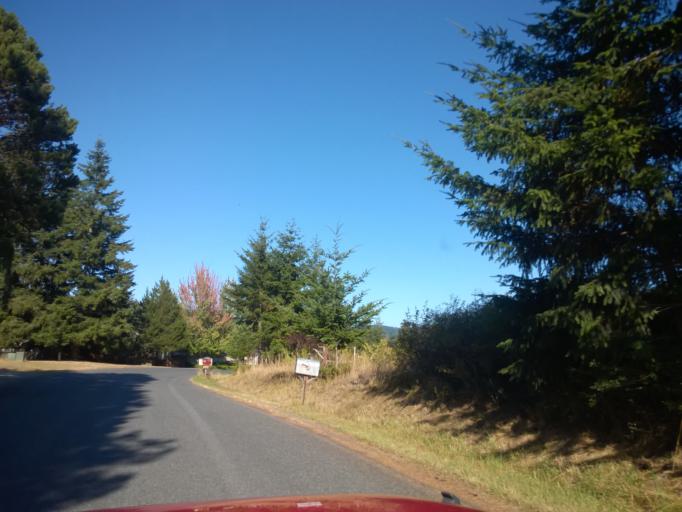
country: US
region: Washington
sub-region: San Juan County
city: Friday Harbor
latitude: 48.5527
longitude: -122.8825
